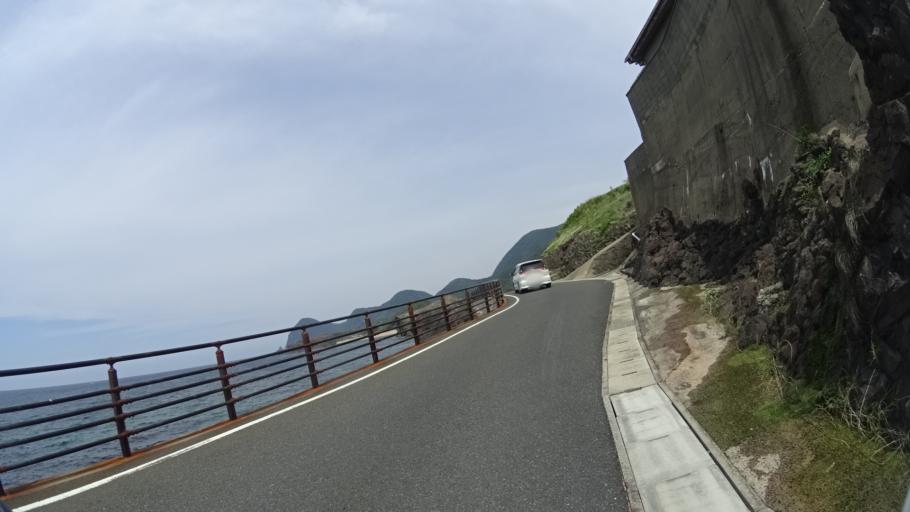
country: JP
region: Kyoto
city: Miyazu
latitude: 35.7411
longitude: 135.0979
